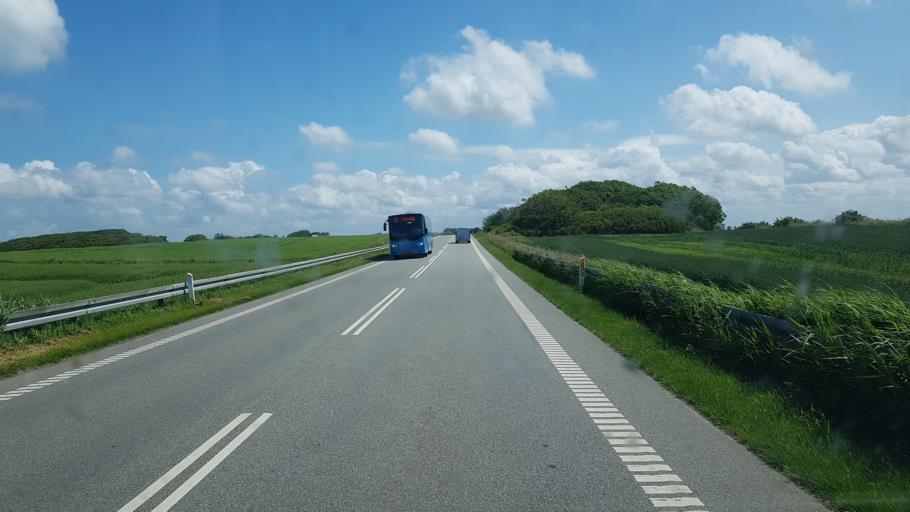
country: DK
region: Central Jutland
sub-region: Lemvig Kommune
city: Lemvig
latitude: 56.5586
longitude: 8.3456
